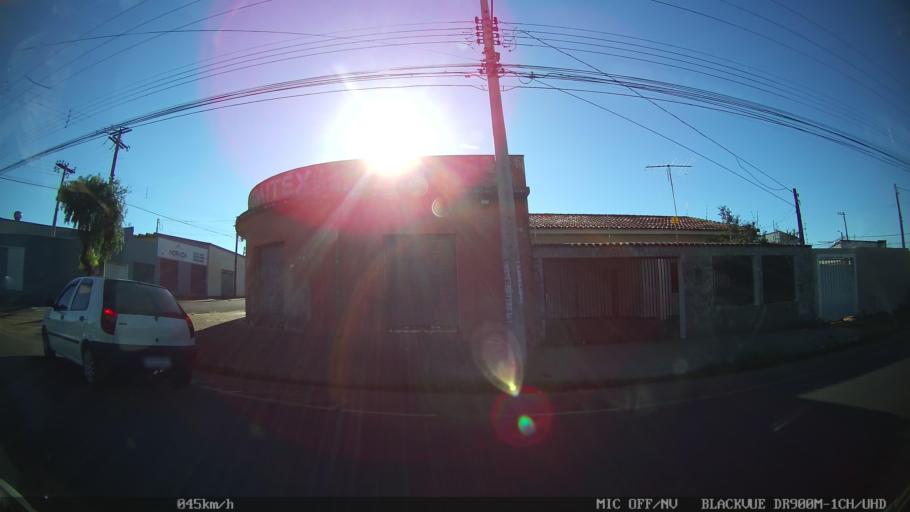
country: BR
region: Sao Paulo
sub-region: Franca
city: Franca
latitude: -20.5802
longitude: -47.3852
